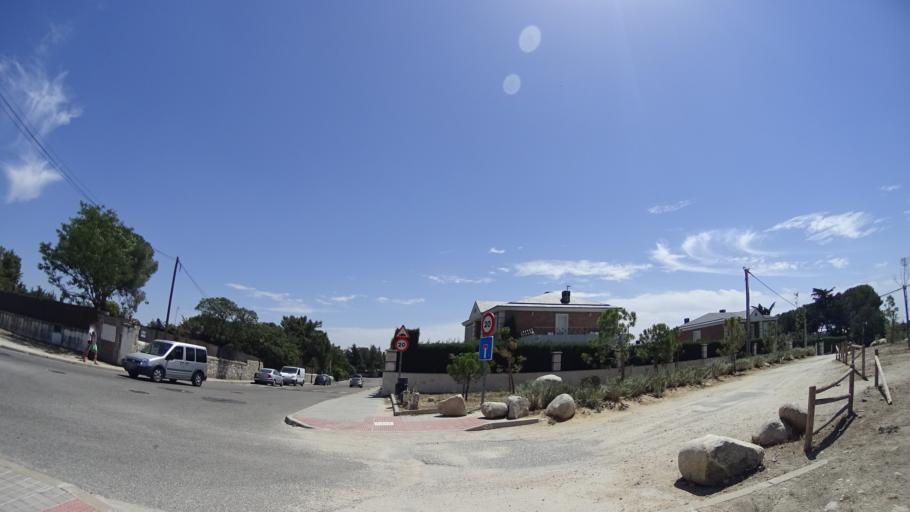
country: ES
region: Madrid
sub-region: Provincia de Madrid
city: Torrelodones
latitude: 40.5776
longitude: -3.9224
